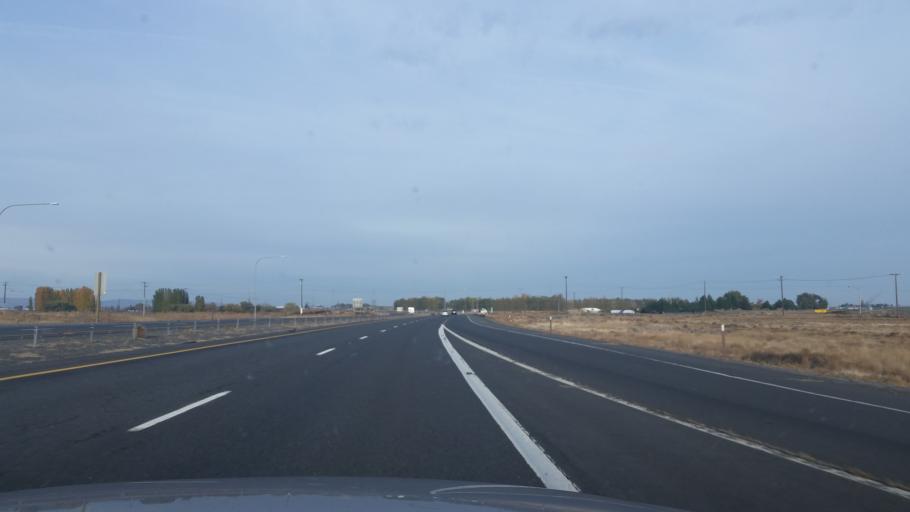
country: US
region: Washington
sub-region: Grant County
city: Quincy
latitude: 47.0858
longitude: -119.8598
